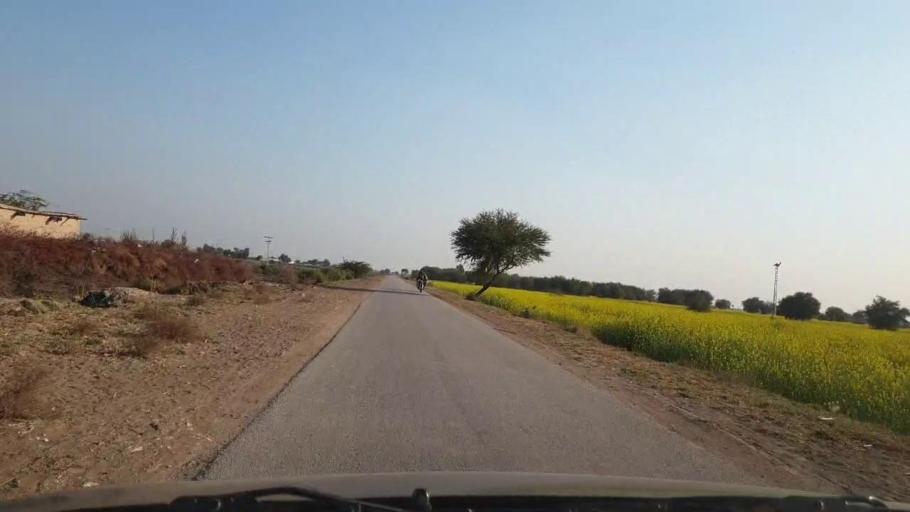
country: PK
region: Sindh
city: Jhol
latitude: 25.9471
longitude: 68.9049
